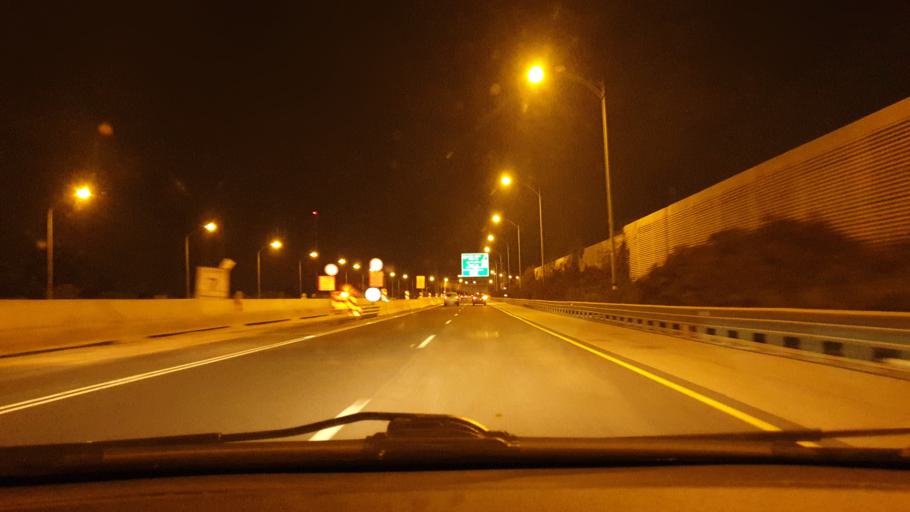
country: IL
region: Central District
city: Ness Ziona
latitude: 31.9291
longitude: 34.8248
